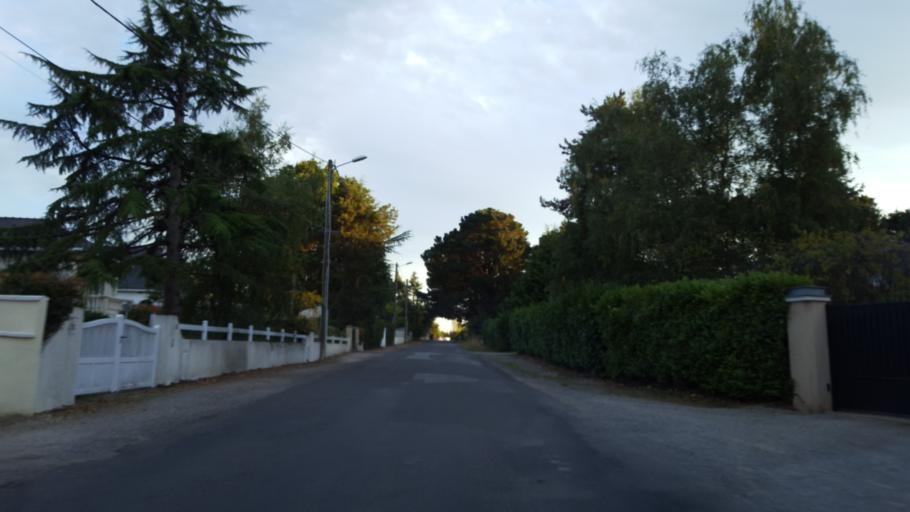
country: FR
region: Pays de la Loire
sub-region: Departement de la Loire-Atlantique
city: Basse-Goulaine
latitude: 47.2116
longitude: -1.4752
